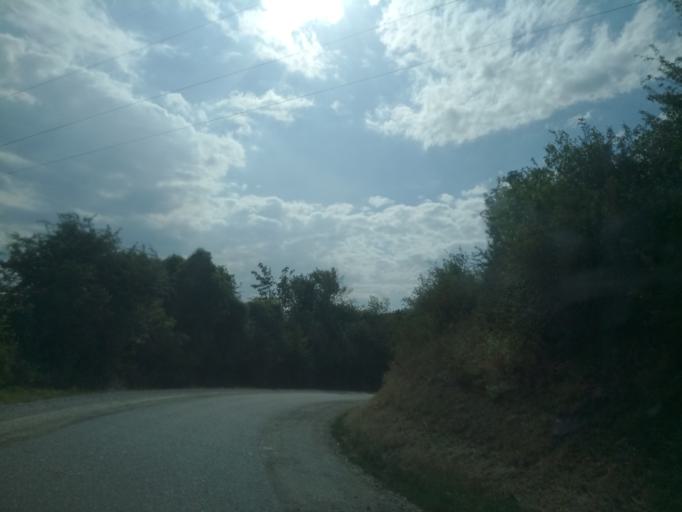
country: RS
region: Autonomna Pokrajina Vojvodina
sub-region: Sremski Okrug
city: Irig
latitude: 45.1057
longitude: 19.9182
